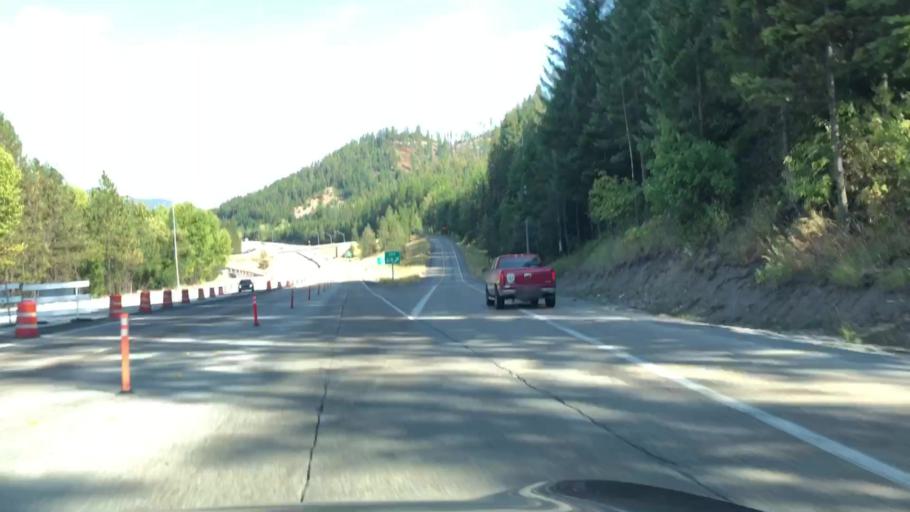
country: US
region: Idaho
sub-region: Shoshone County
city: Wallace
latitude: 47.4687
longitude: -115.7915
